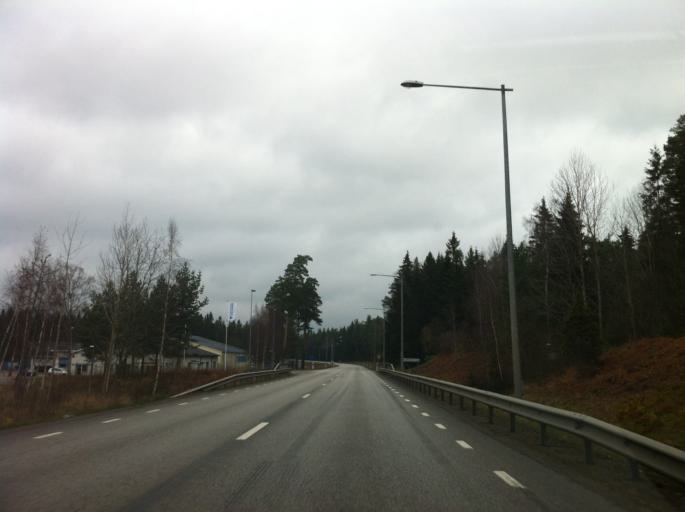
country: SE
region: Joenkoeping
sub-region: Vetlanda Kommun
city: Vetlanda
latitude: 57.4131
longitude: 15.0620
